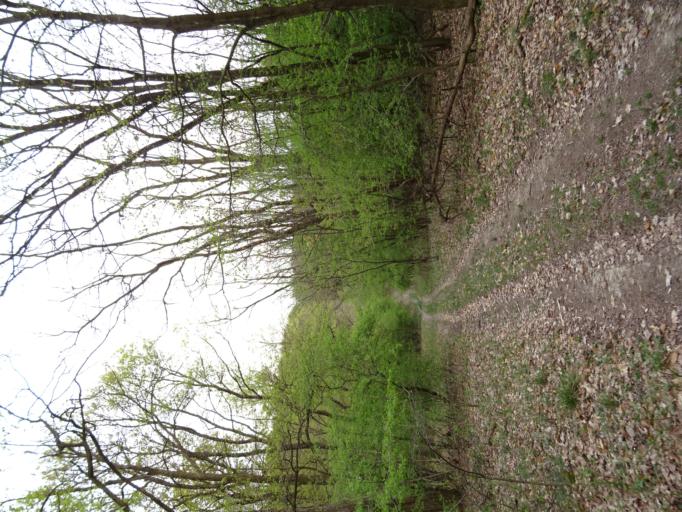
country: SK
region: Kosicky
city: Moldava nad Bodvou
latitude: 48.5243
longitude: 20.9762
